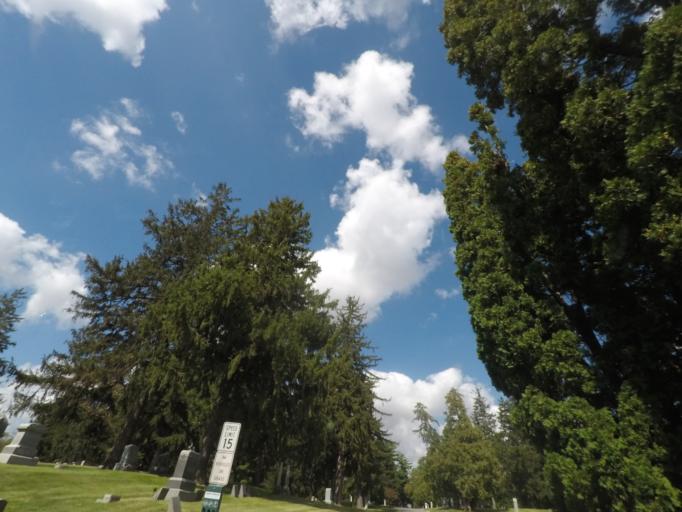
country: US
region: Iowa
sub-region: Story County
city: Nevada
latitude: 42.0197
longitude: -93.4617
